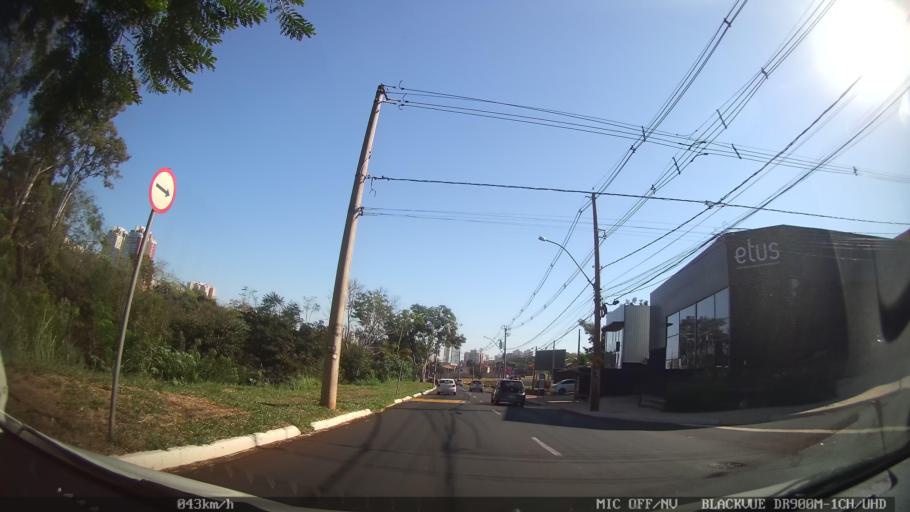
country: BR
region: Sao Paulo
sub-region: Ribeirao Preto
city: Ribeirao Preto
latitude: -21.2197
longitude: -47.7901
